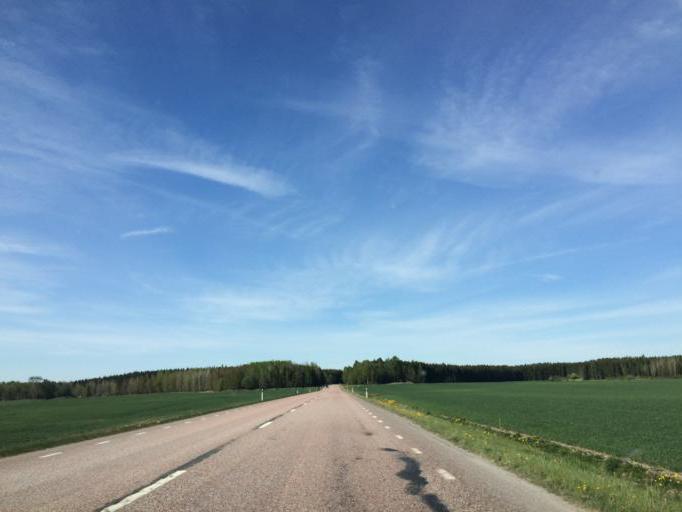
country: SE
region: Soedermanland
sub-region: Katrineholms Kommun
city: Katrineholm
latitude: 59.0201
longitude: 16.2143
